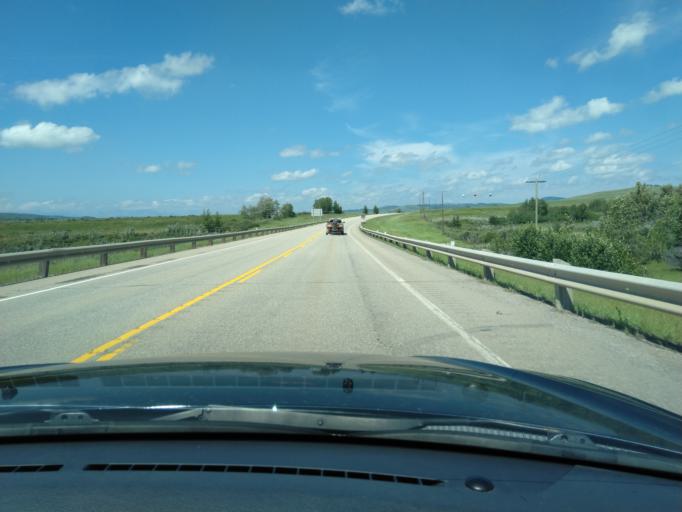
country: CA
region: Alberta
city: Cochrane
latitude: 51.2082
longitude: -114.5188
